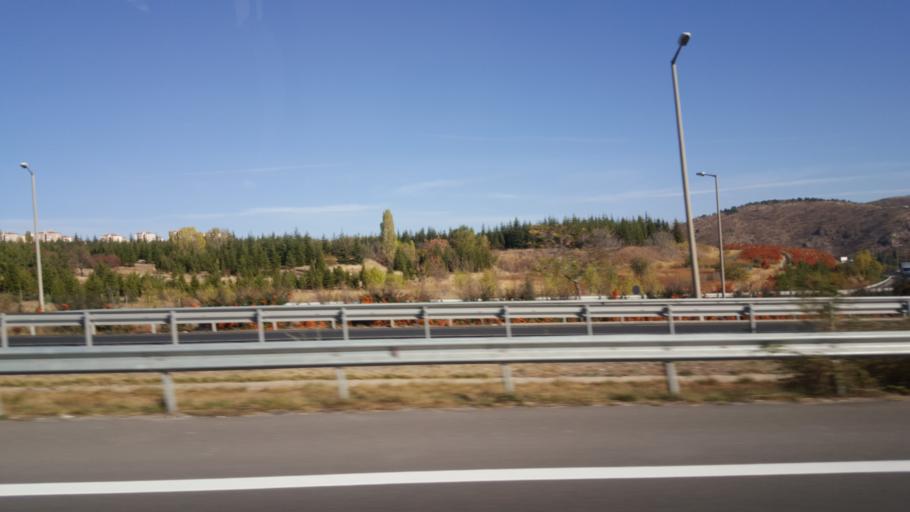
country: TR
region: Ankara
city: Mamak
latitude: 40.0177
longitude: 32.8936
